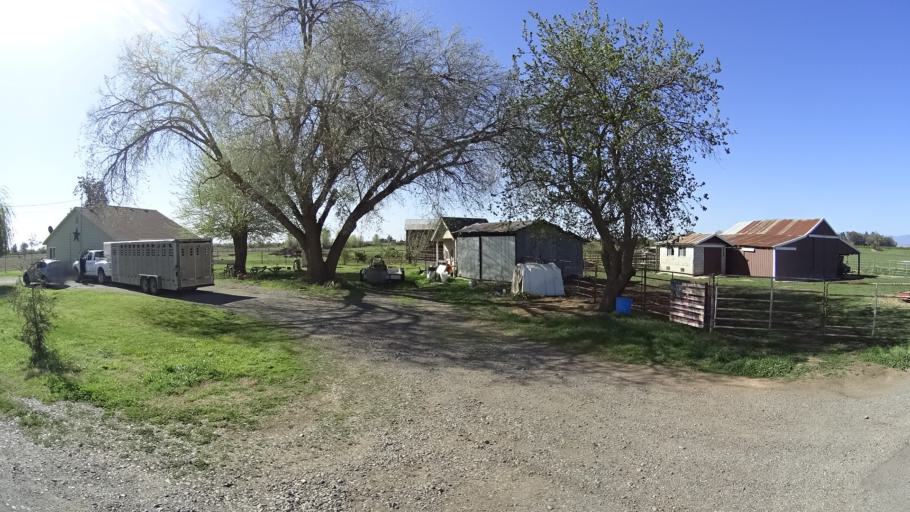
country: US
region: California
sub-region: Glenn County
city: Orland
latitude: 39.7369
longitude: -122.2341
